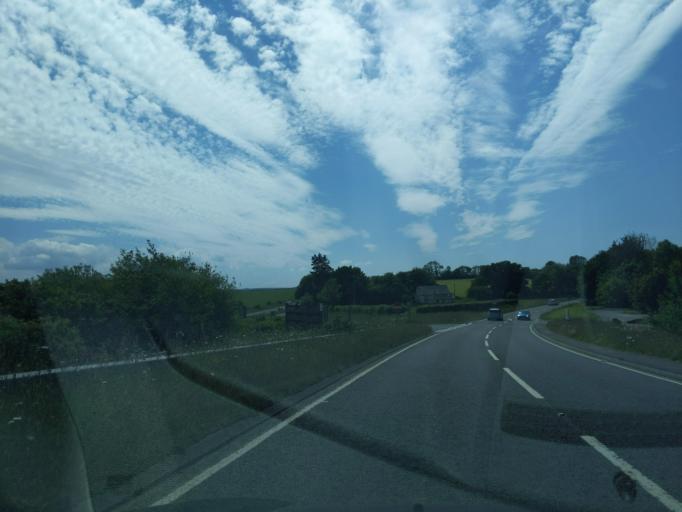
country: GB
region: England
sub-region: Cornwall
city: Trewen
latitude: 50.6231
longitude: -4.4201
